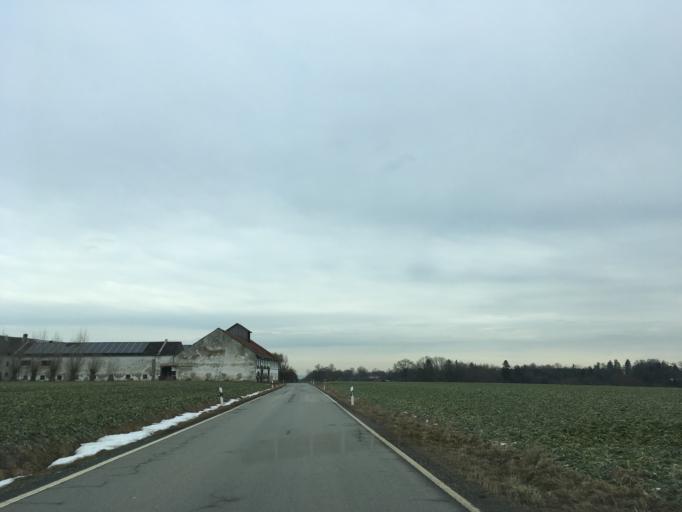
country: DE
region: Bavaria
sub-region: Upper Bavaria
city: Kraiburg am Inn
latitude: 48.1728
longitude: 12.4198
